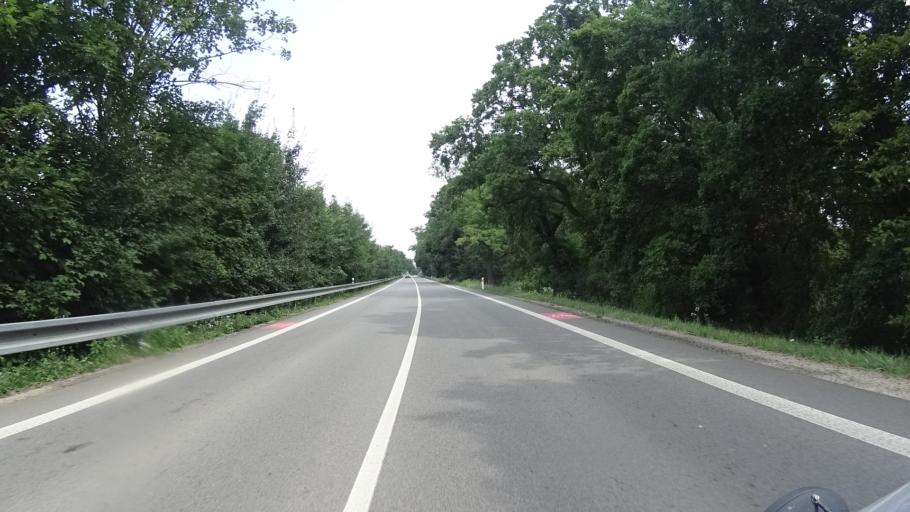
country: CZ
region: South Moravian
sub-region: Okres Breclav
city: Lednice
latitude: 48.8101
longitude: 16.8049
